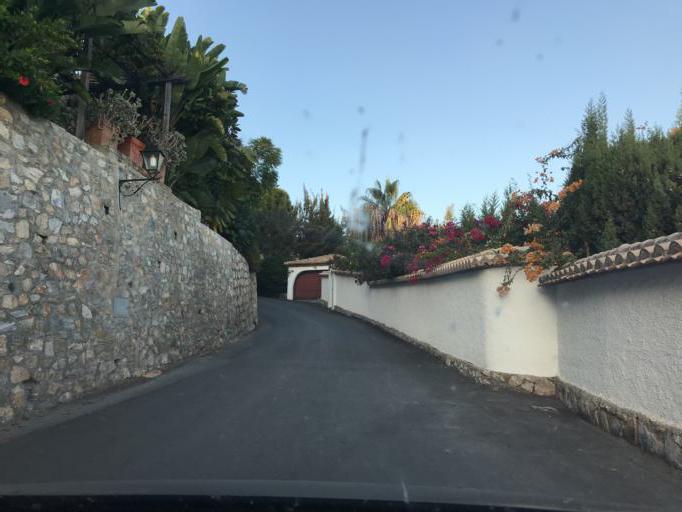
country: ES
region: Andalusia
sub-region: Provincia de Granada
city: Salobrena
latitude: 36.7438
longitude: -3.6155
